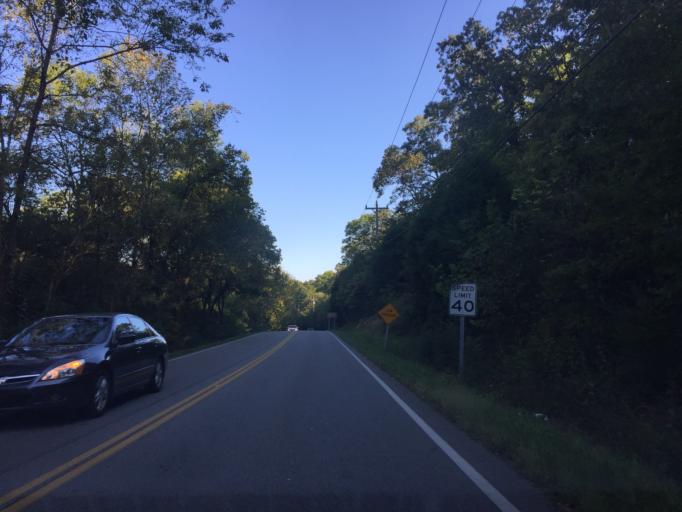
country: US
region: Tennessee
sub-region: Hamilton County
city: Harrison
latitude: 35.1136
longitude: -85.0822
